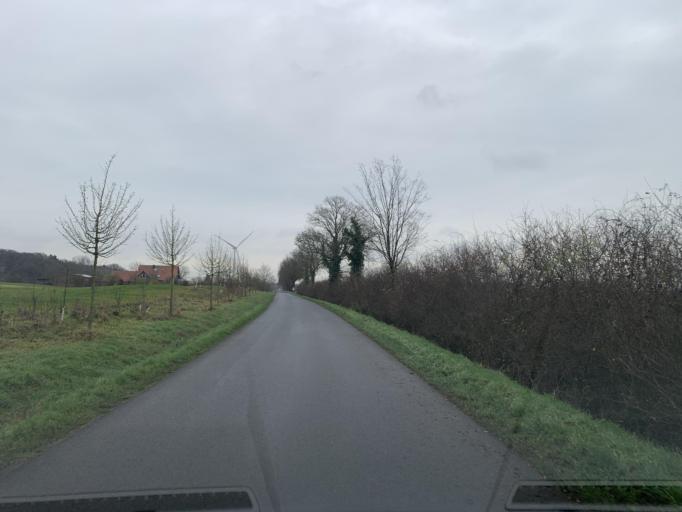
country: DE
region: North Rhine-Westphalia
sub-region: Regierungsbezirk Munster
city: Senden
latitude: 51.8969
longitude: 7.5511
